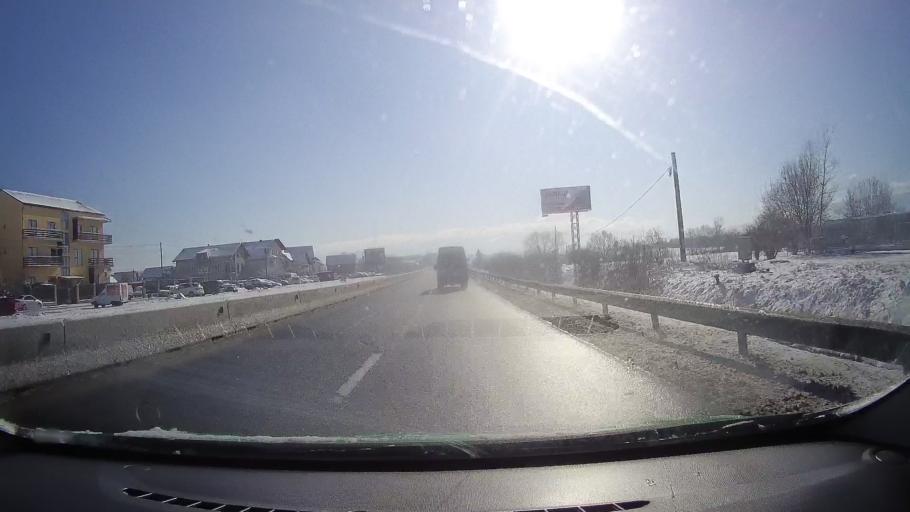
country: RO
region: Sibiu
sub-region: Comuna Selimbar
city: Selimbar
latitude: 45.7686
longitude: 24.1829
